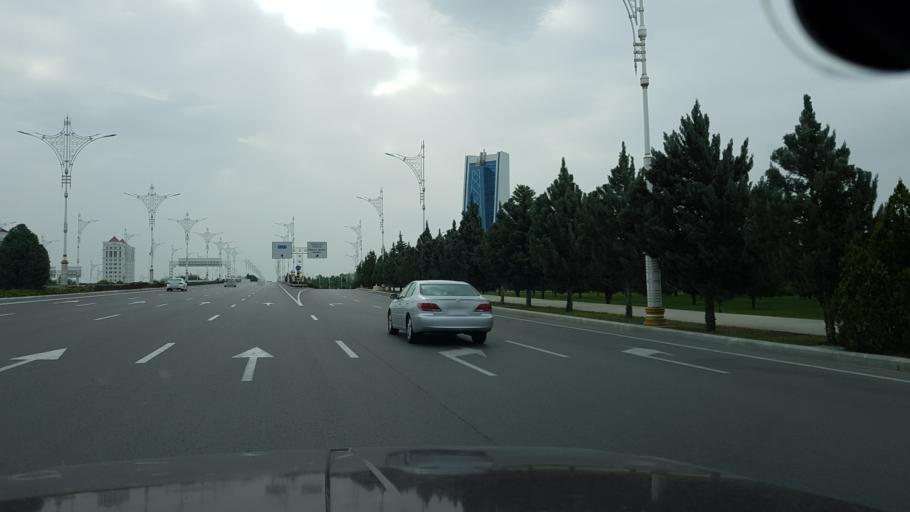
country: TM
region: Ahal
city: Ashgabat
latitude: 37.8789
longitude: 58.3824
